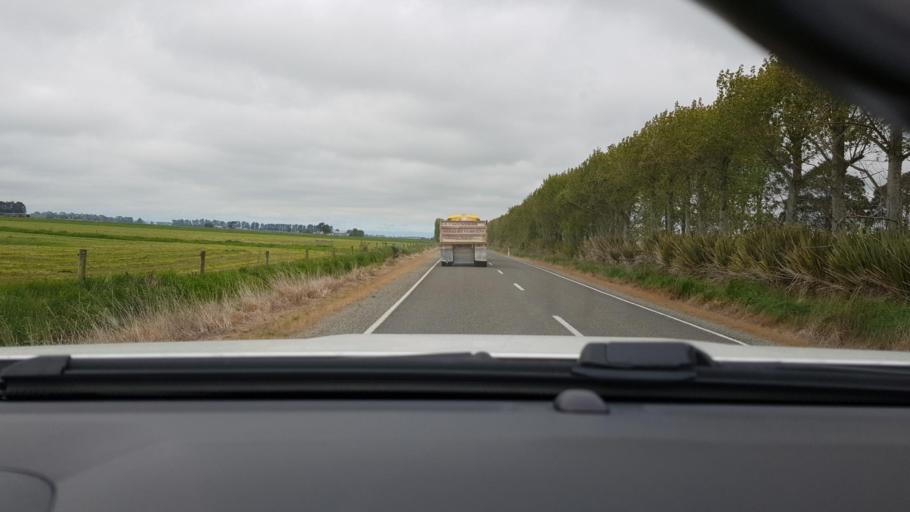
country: NZ
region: Otago
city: Oamaru
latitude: -44.9648
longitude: 170.9432
